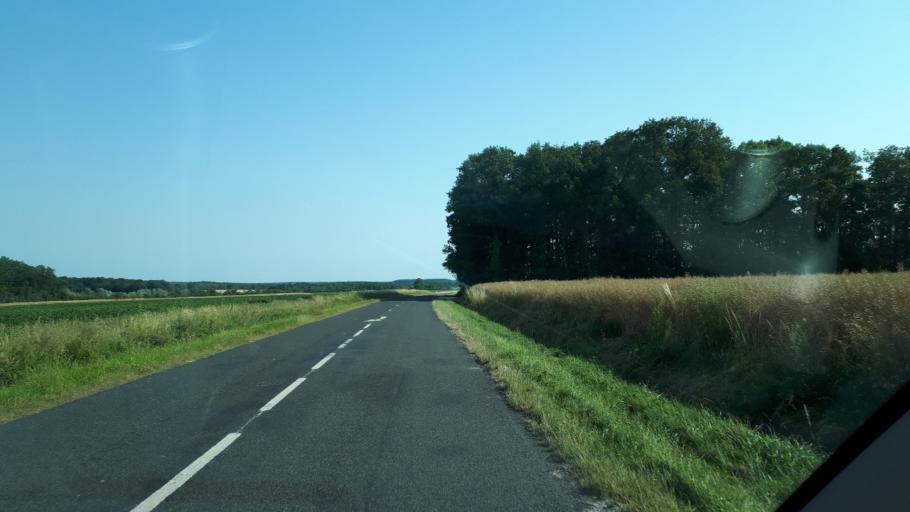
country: FR
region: Centre
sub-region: Departement du Loir-et-Cher
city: La Ville-aux-Clercs
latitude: 47.9515
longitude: 1.0809
